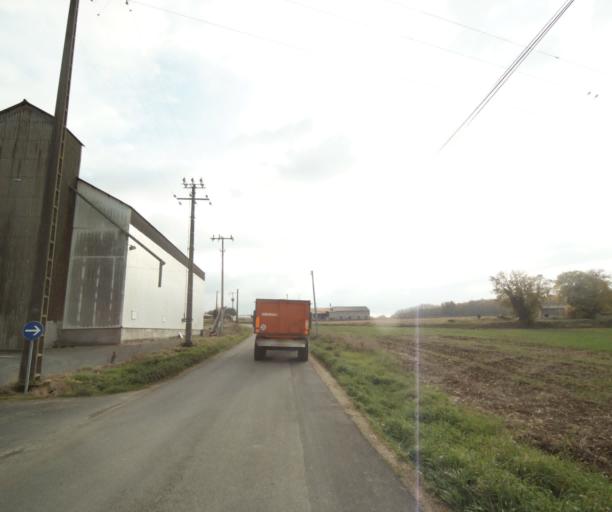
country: FR
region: Poitou-Charentes
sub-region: Departement de la Charente-Maritime
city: Saint-Georges-des-Coteaux
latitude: 45.7750
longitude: -0.7240
